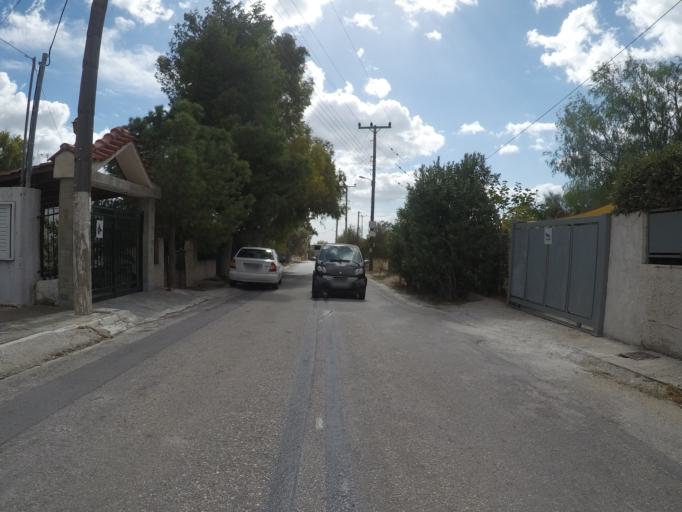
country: GR
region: Attica
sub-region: Nomarchia Anatolikis Attikis
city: Agios Dimitrios Kropias
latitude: 37.8057
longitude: 23.8676
